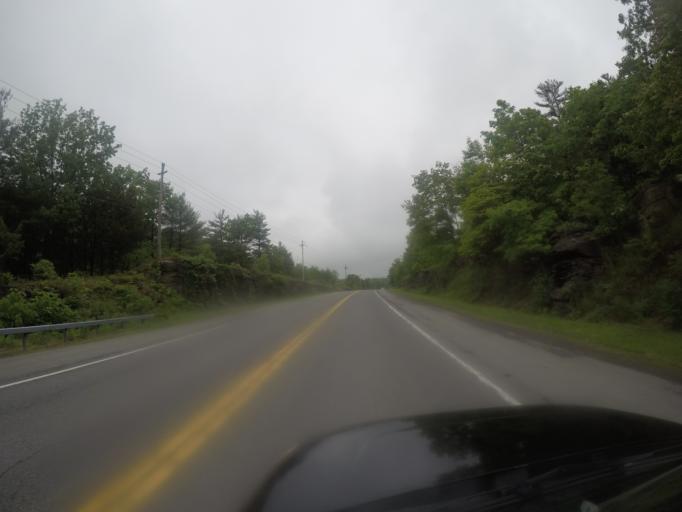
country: US
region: New York
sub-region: Ulster County
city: West Hurley
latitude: 42.0010
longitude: -74.1386
